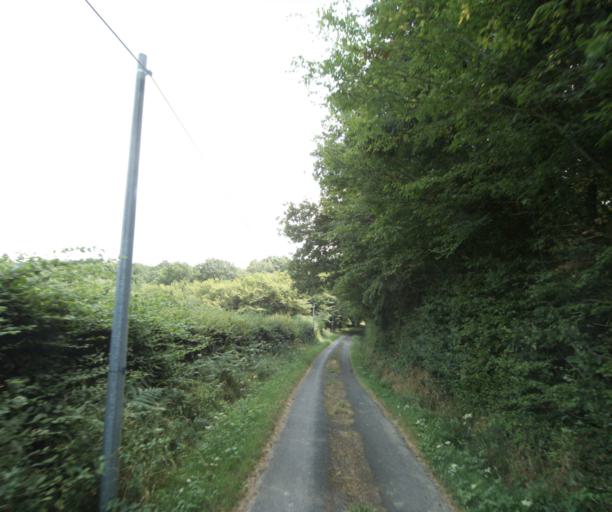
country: FR
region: Bourgogne
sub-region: Departement de Saone-et-Loire
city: Gueugnon
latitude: 46.6050
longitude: 4.0216
